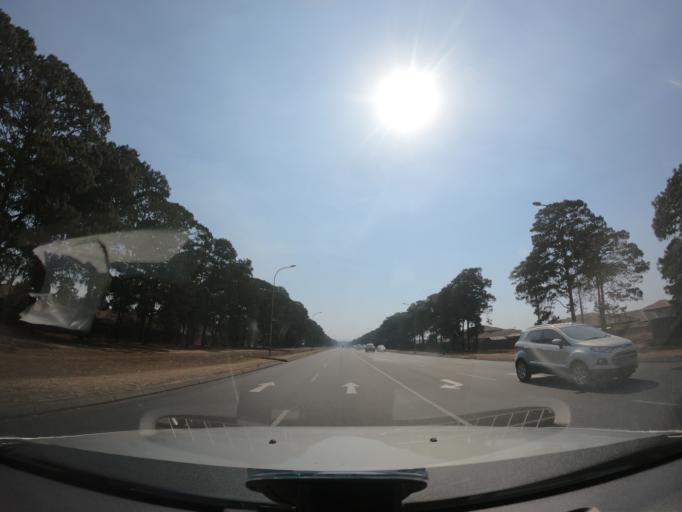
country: ZA
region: Mpumalanga
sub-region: Nkangala District Municipality
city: Middelburg
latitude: -25.8013
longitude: 29.4621
